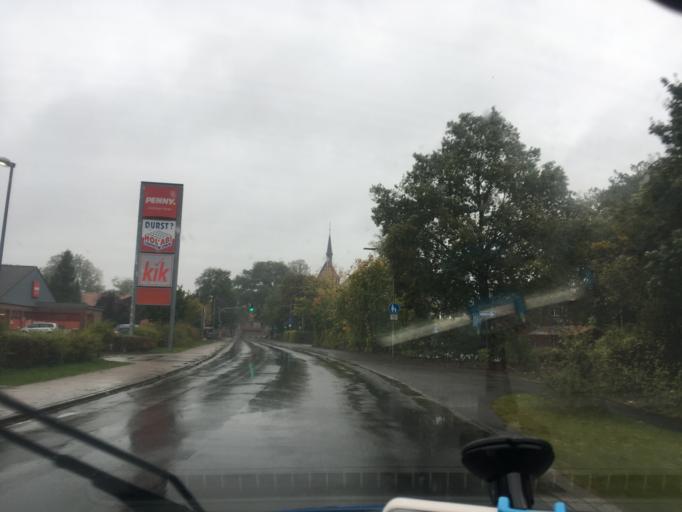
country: DE
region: Lower Saxony
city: Bispingen
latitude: 53.0799
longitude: 9.9967
